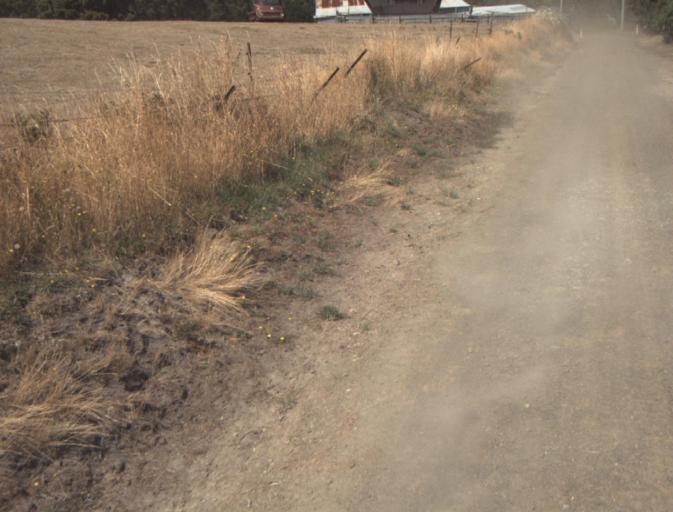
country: AU
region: Tasmania
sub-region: Launceston
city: Mayfield
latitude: -41.2519
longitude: 147.1737
